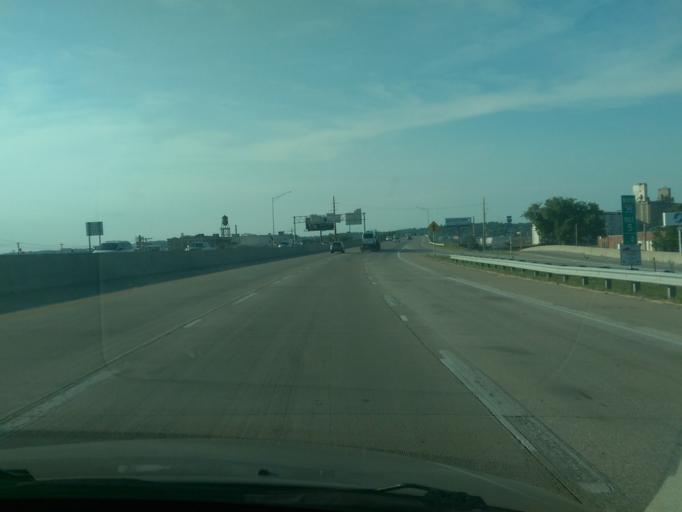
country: US
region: Missouri
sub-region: Clay County
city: North Kansas City
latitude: 39.1281
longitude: -94.5678
